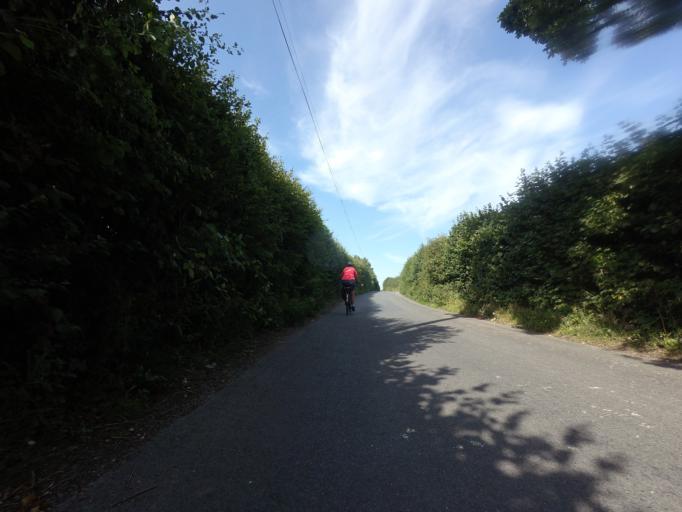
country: GB
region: England
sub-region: East Sussex
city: Rye
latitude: 50.9907
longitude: 0.6774
